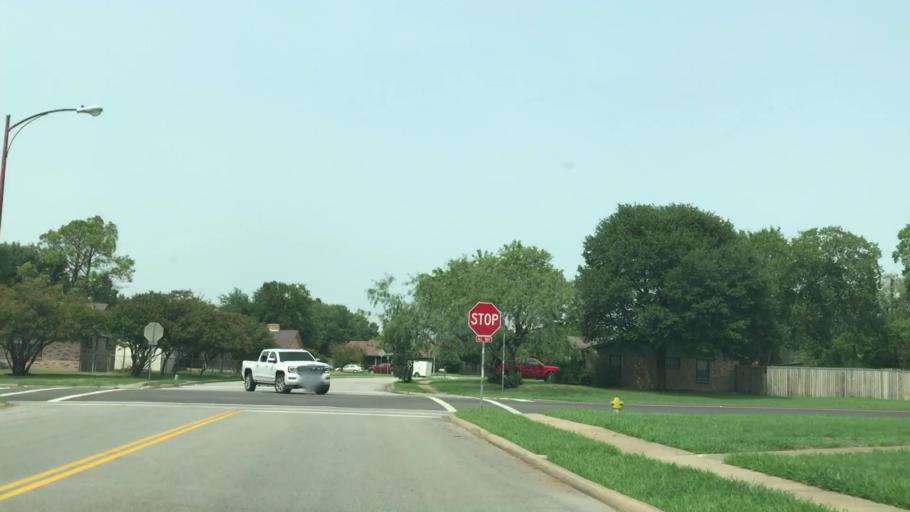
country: US
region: Texas
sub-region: Dallas County
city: Irving
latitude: 32.8472
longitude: -97.0013
